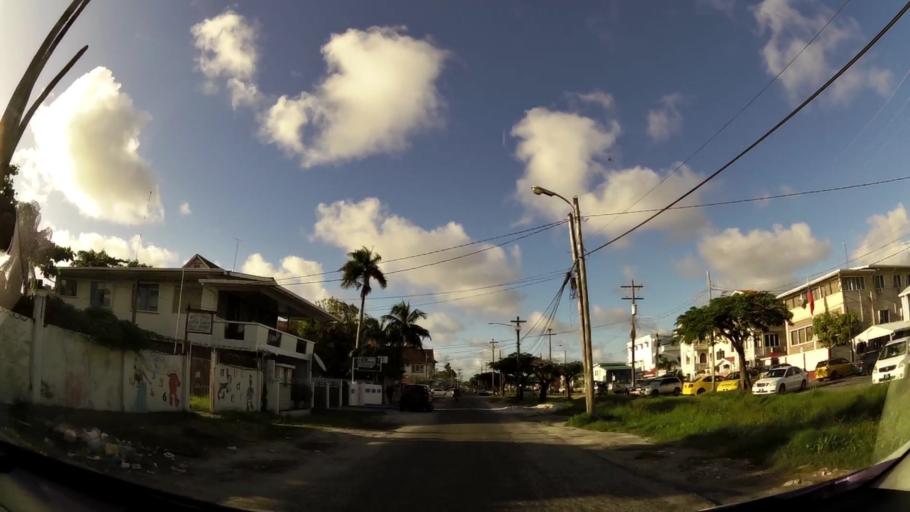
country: GY
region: Demerara-Mahaica
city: Georgetown
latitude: 6.8127
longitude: -58.1585
